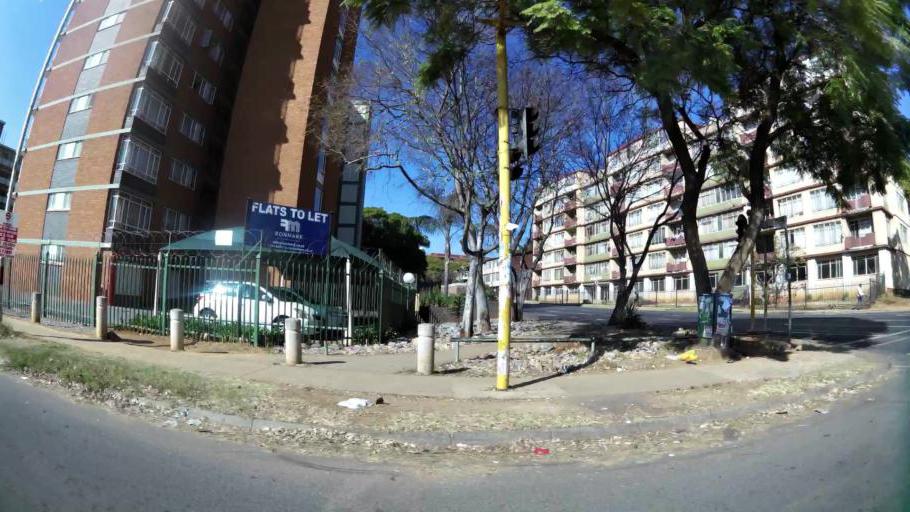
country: ZA
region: Gauteng
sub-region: City of Tshwane Metropolitan Municipality
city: Pretoria
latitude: -25.7579
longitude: 28.2003
